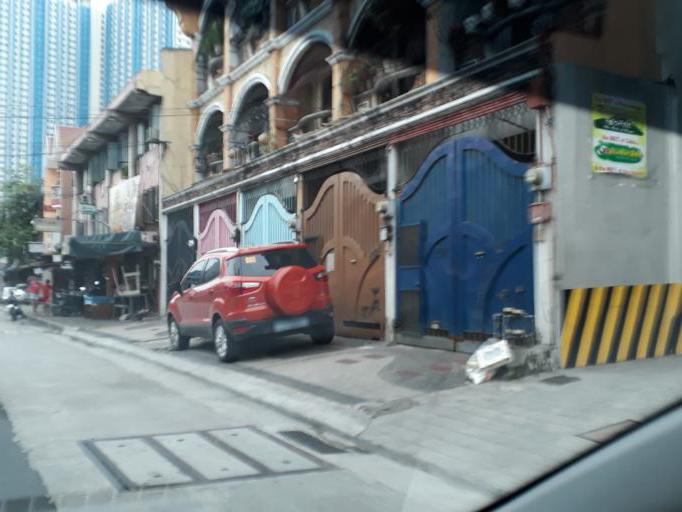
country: PH
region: Metro Manila
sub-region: City of Manila
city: Manila
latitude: 14.6214
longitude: 121.0000
